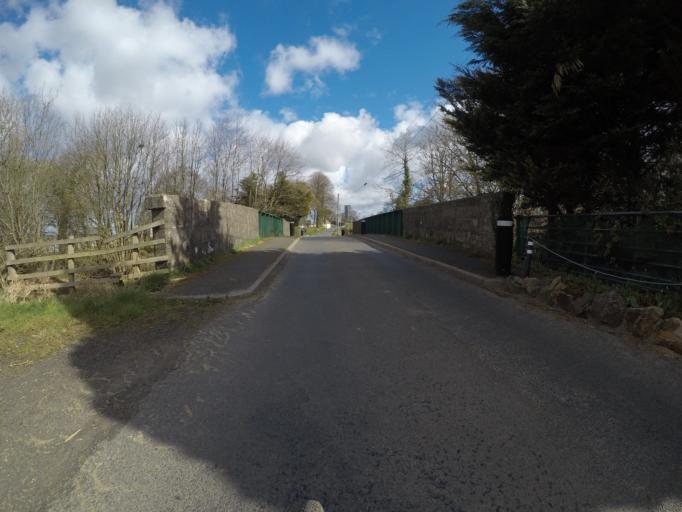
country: GB
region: Scotland
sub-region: North Ayrshire
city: Beith
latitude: 55.7189
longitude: -4.6194
